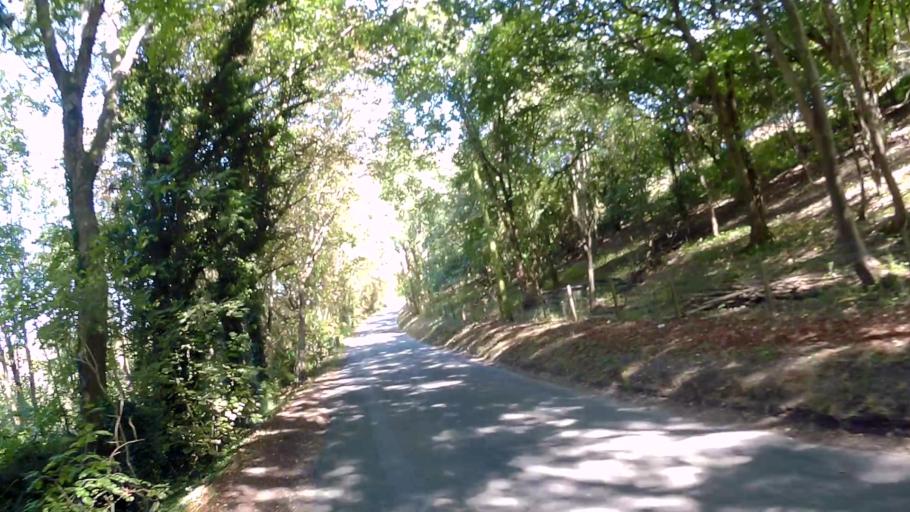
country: GB
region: England
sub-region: Hampshire
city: Andover
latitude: 51.1519
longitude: -1.4509
